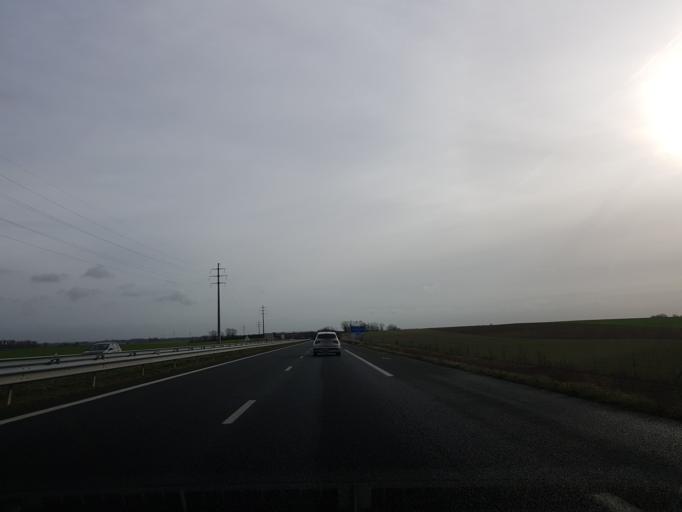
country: FR
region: Champagne-Ardenne
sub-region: Departement de l'Aube
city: Saint-Germain
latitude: 48.2456
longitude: 3.9929
